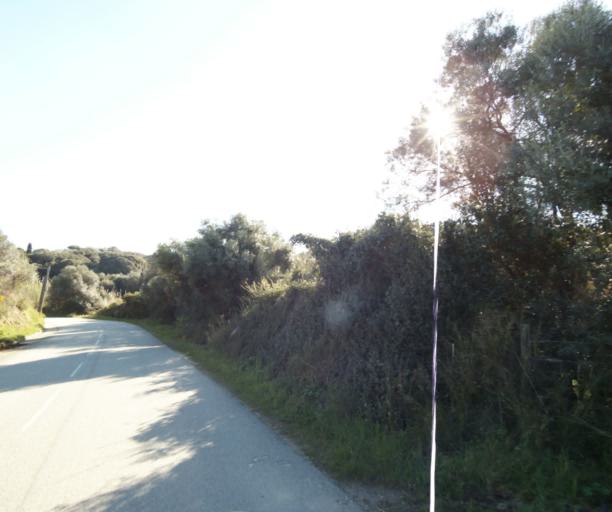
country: FR
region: Corsica
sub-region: Departement de la Corse-du-Sud
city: Propriano
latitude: 41.6664
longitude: 8.8944
